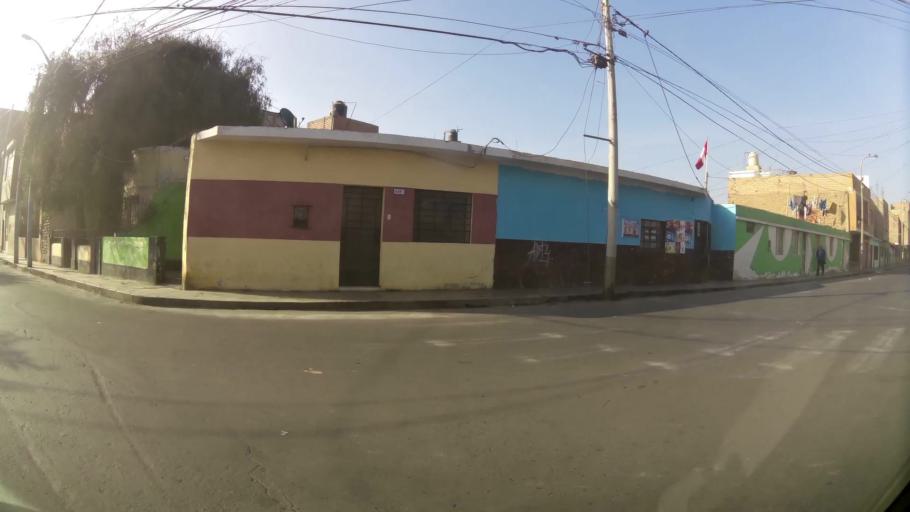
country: PE
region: Lima
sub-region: Huaura
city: Huacho
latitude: -11.1063
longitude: -77.6125
